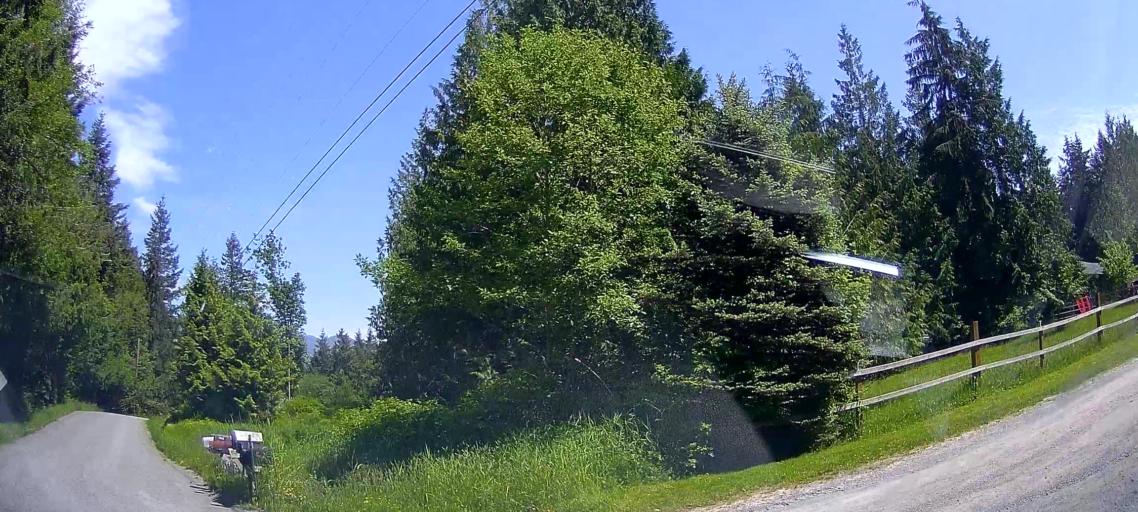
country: US
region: Washington
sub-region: Skagit County
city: Big Lake
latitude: 48.3777
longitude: -122.2662
